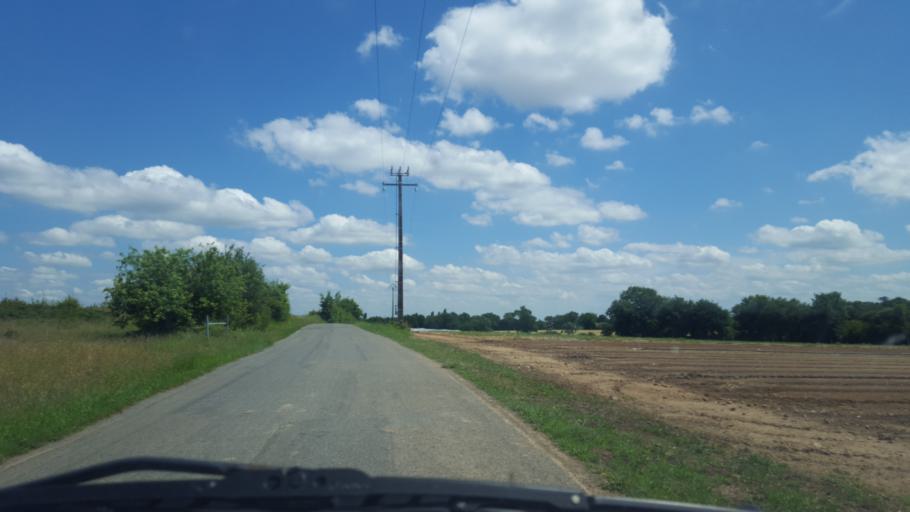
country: FR
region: Pays de la Loire
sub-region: Departement de la Loire-Atlantique
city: Saint-Philbert-de-Grand-Lieu
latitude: 47.0242
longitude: -1.6297
